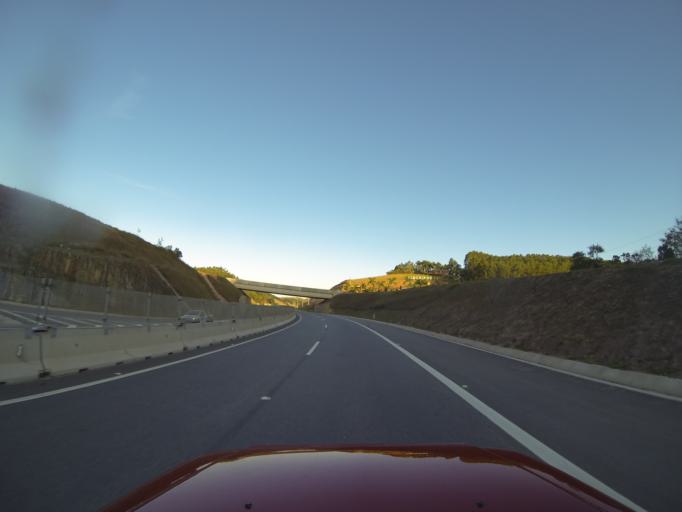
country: BR
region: Sao Paulo
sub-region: Caraguatatuba
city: Caraguatatuba
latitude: -23.4510
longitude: -45.6024
